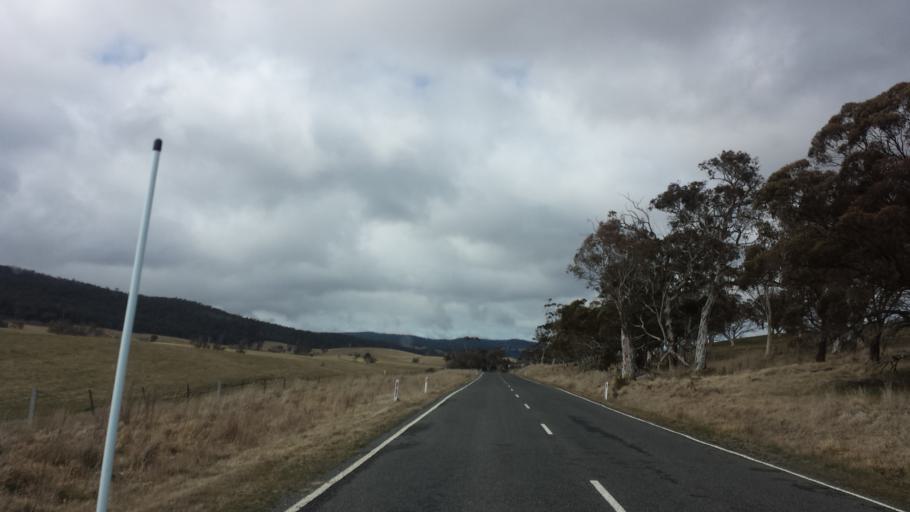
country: AU
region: Victoria
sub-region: Alpine
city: Mount Beauty
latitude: -37.1233
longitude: 147.4483
